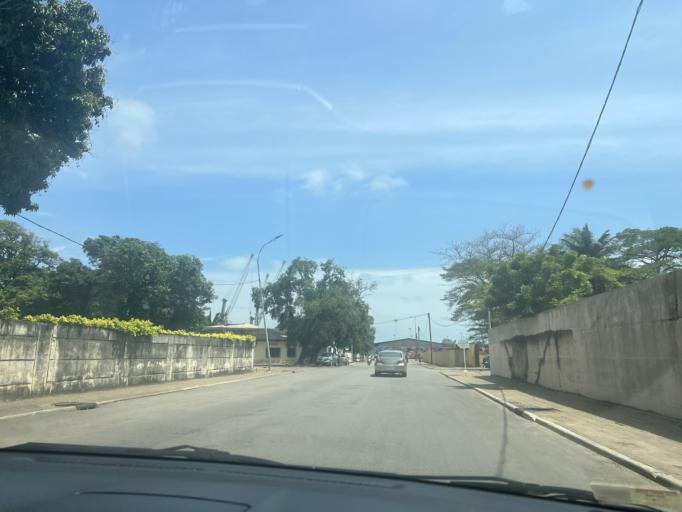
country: BJ
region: Littoral
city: Cotonou
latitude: 6.3521
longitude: 2.4176
